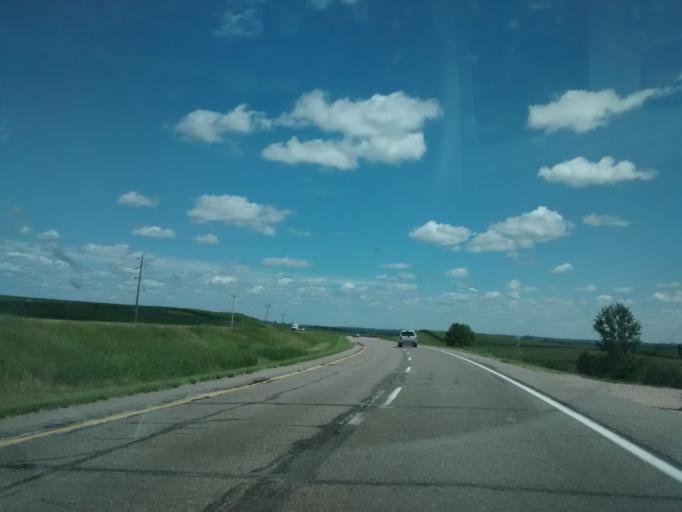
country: US
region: Iowa
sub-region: Woodbury County
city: Moville
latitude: 42.4759
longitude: -96.1025
